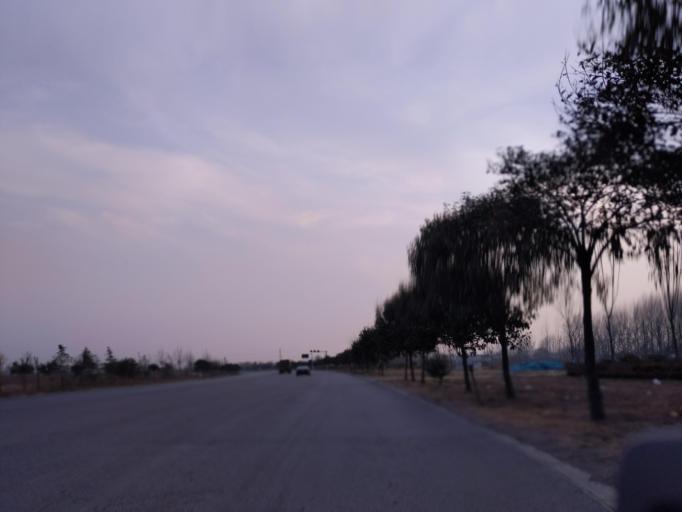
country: CN
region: Henan Sheng
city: Puyang
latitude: 35.8141
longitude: 114.9672
